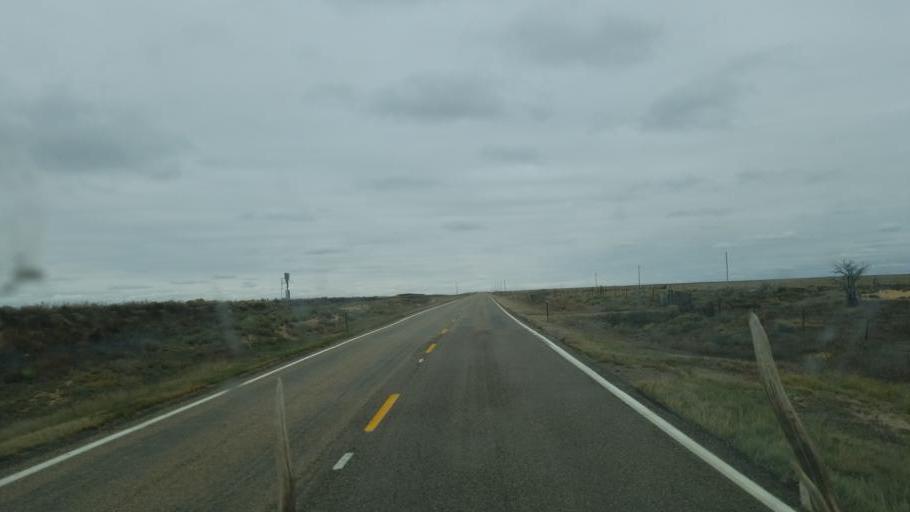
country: US
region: Colorado
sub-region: Crowley County
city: Ordway
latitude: 38.2404
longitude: -103.6304
